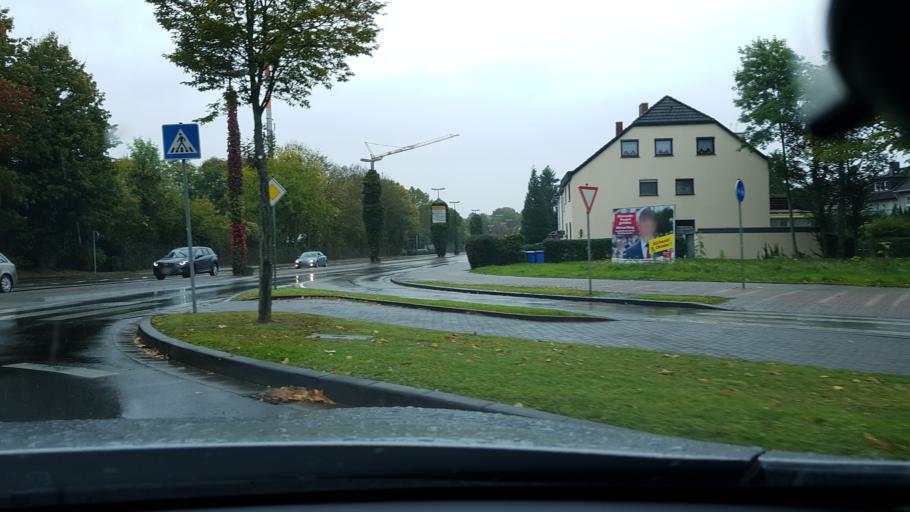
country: DE
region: Rheinland-Pfalz
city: Neuwied
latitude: 50.4324
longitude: 7.4569
